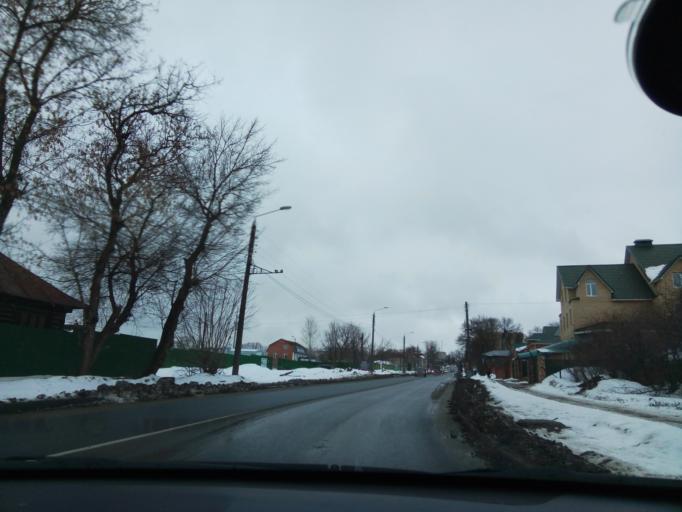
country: RU
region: Chuvashia
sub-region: Cheboksarskiy Rayon
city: Cheboksary
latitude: 56.1361
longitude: 47.2366
